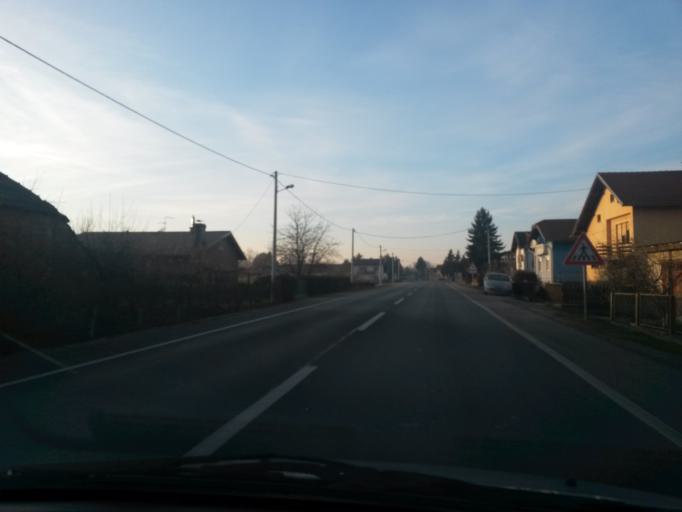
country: HR
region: Varazdinska
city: Jalzabet
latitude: 46.3015
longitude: 16.4771
